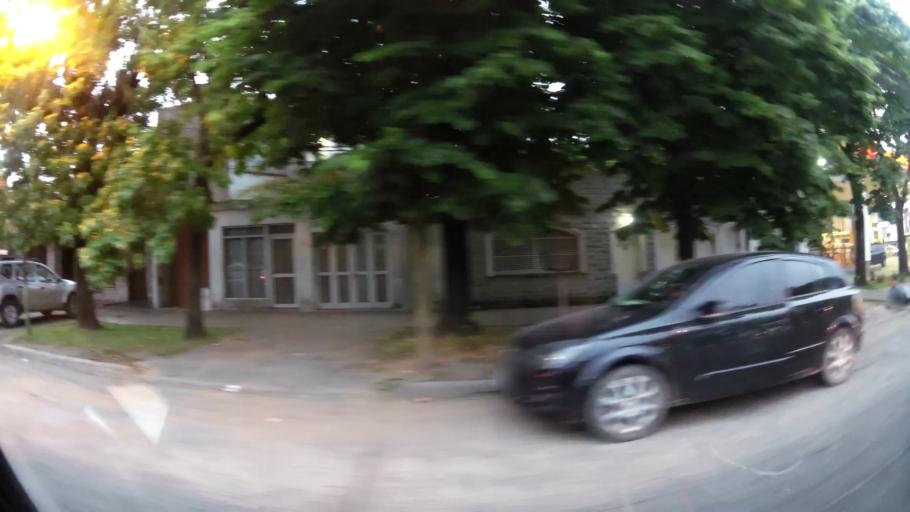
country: AR
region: Buenos Aires
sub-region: Partido de La Plata
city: La Plata
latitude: -34.9006
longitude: -57.9699
